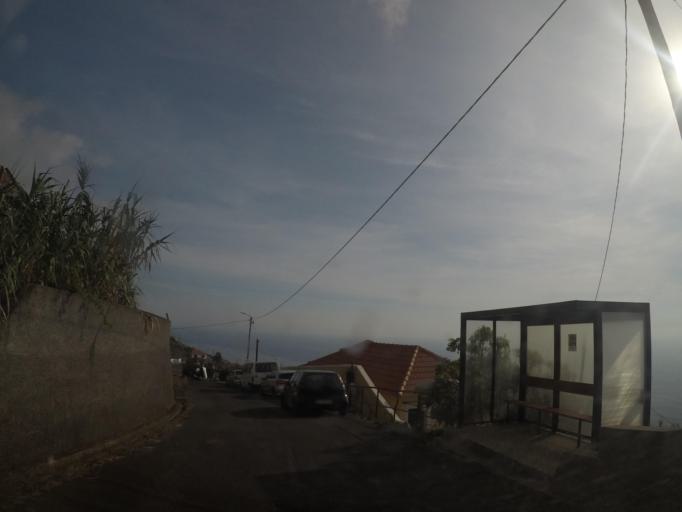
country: PT
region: Madeira
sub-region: Calheta
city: Faja da Ovelha
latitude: 32.7772
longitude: -17.2382
